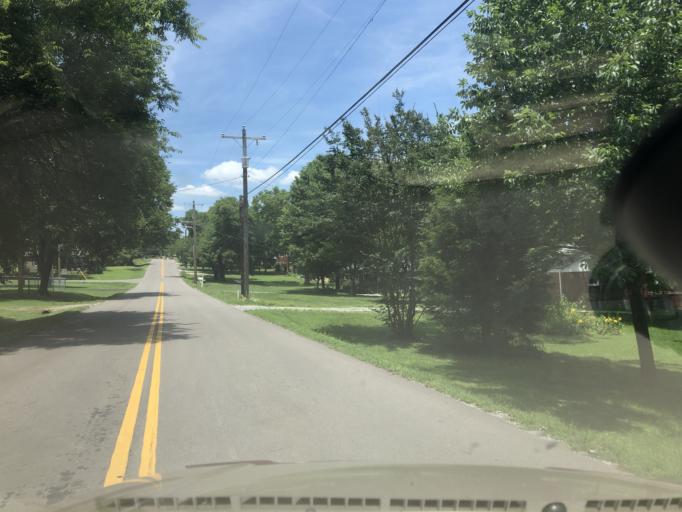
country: US
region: Tennessee
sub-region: Davidson County
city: Lakewood
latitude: 36.2560
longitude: -86.6955
